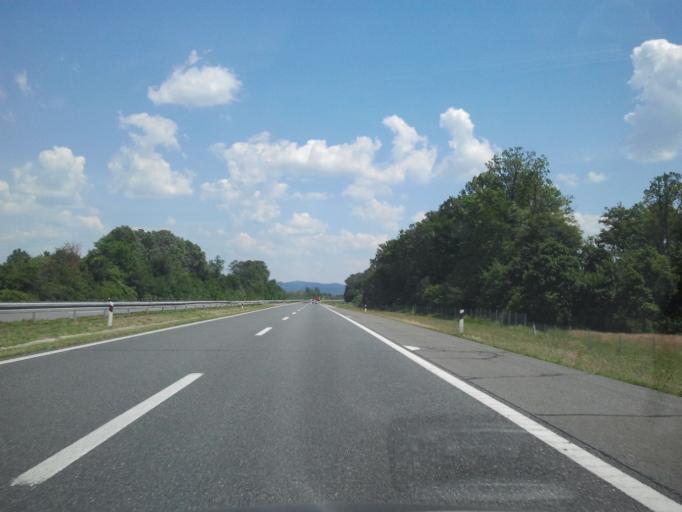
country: HR
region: Brodsko-Posavska
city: Vrbova
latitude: 45.1916
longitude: 17.6074
